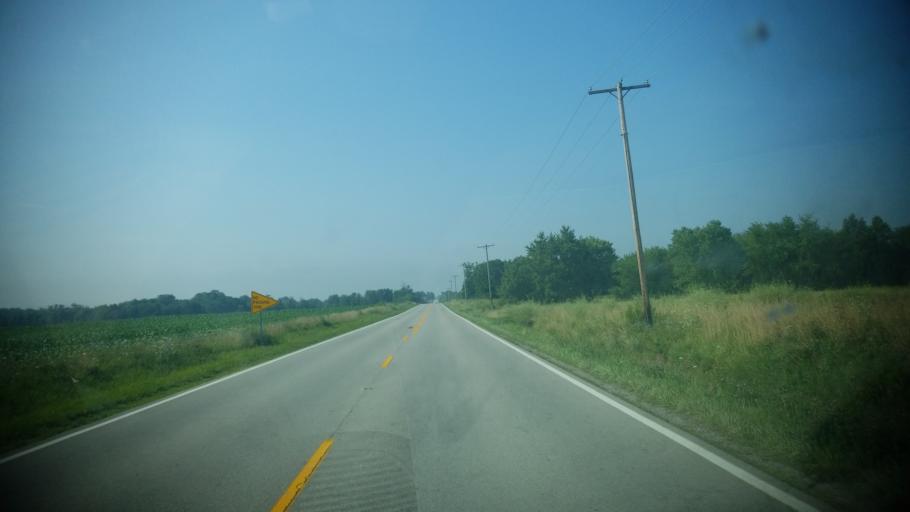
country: US
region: Illinois
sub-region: Clay County
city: Flora
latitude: 38.6022
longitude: -88.4385
